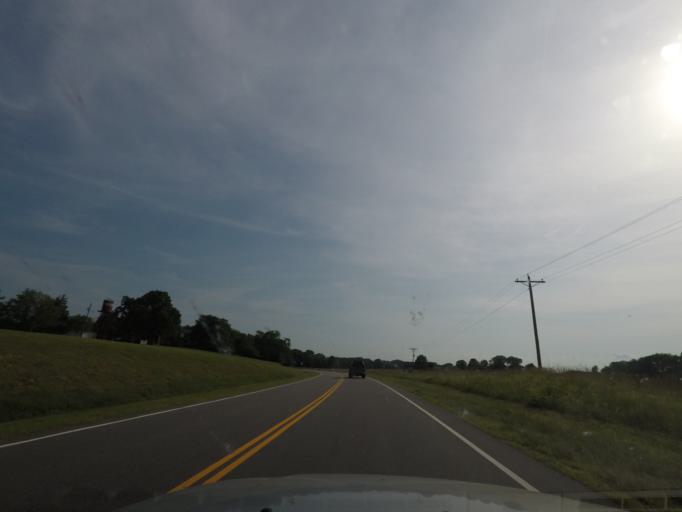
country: US
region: Virginia
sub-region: Mecklenburg County
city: Chase City
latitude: 36.7852
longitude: -78.6141
